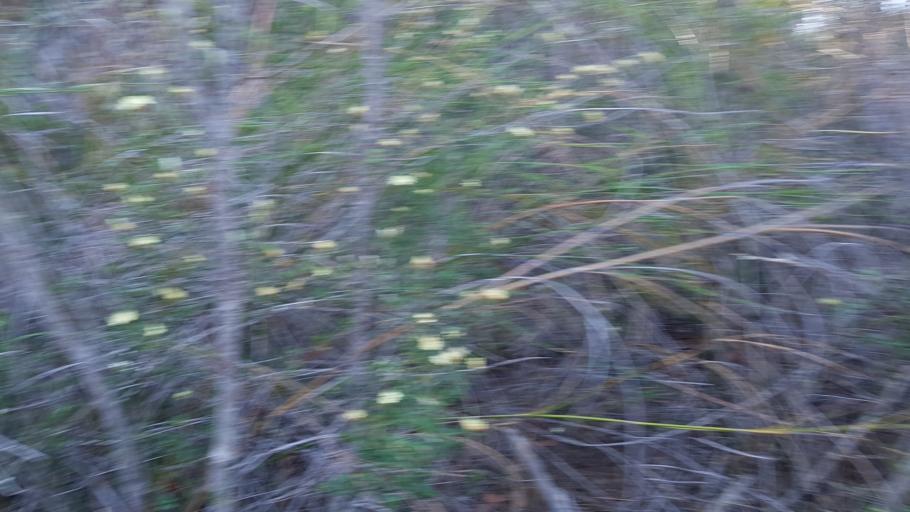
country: AU
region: New South Wales
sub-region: Hornsby Shire
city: Berowra
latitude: -33.5828
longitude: 151.2138
